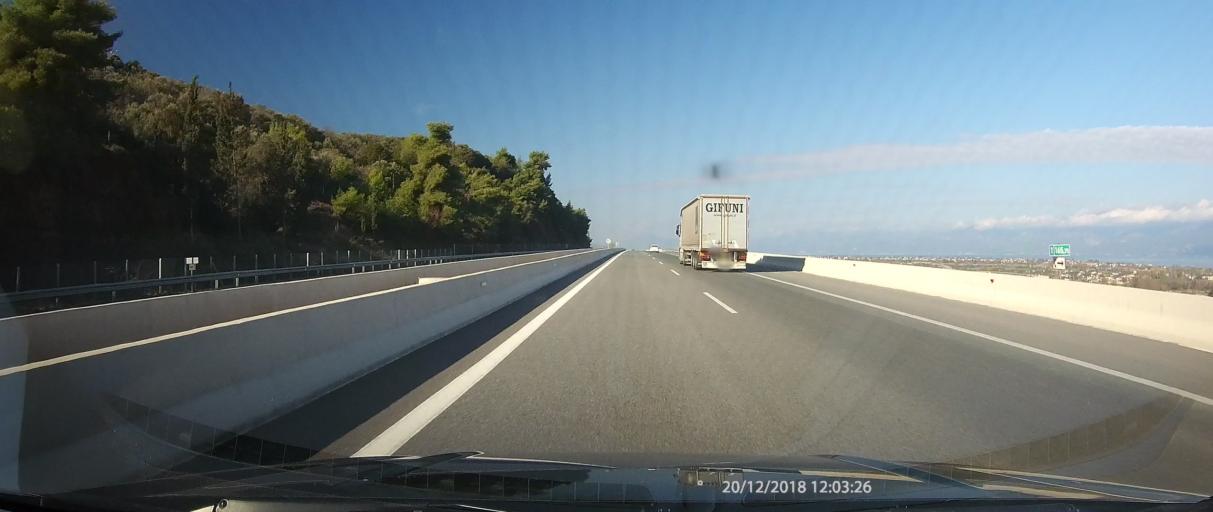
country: GR
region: West Greece
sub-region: Nomos Achaias
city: Temeni
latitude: 38.2015
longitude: 22.1472
